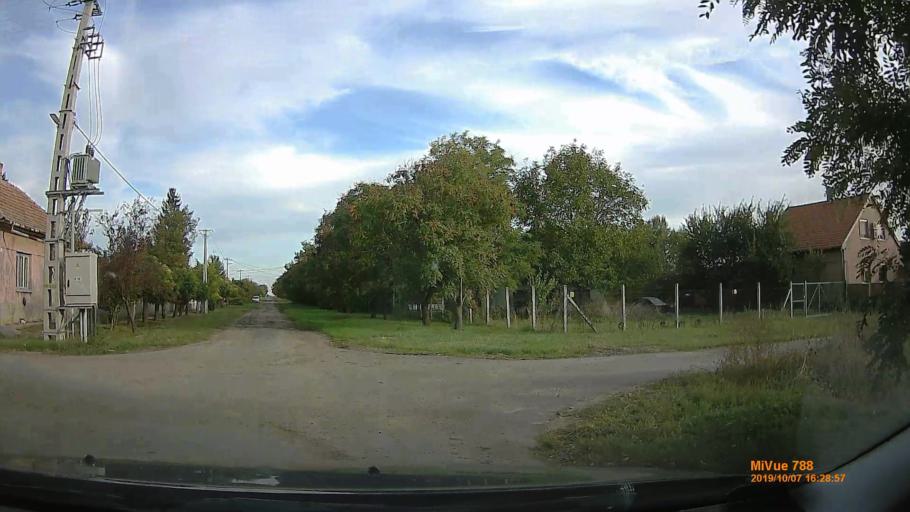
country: HU
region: Bekes
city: Szarvas
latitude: 46.8198
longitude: 20.6493
